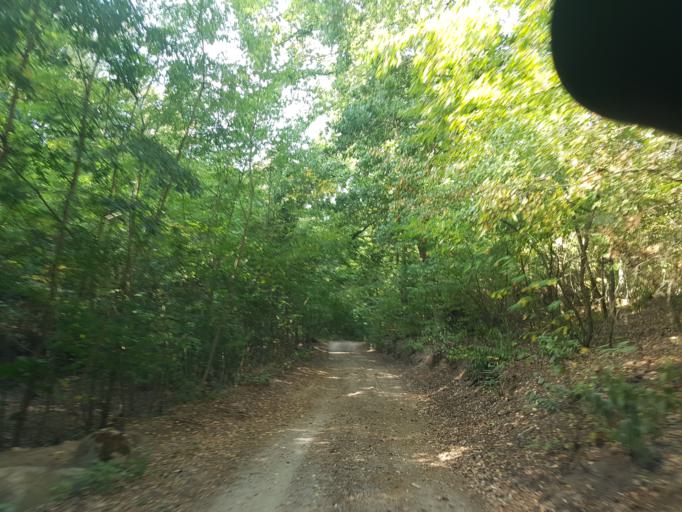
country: DE
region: Brandenburg
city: Belzig
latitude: 52.1506
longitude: 12.5773
